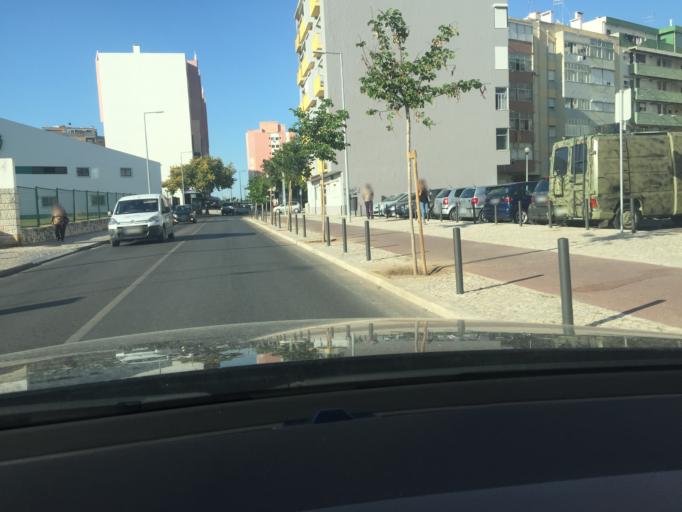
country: PT
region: Setubal
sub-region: Setubal
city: Setubal
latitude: 38.5307
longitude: -8.8899
